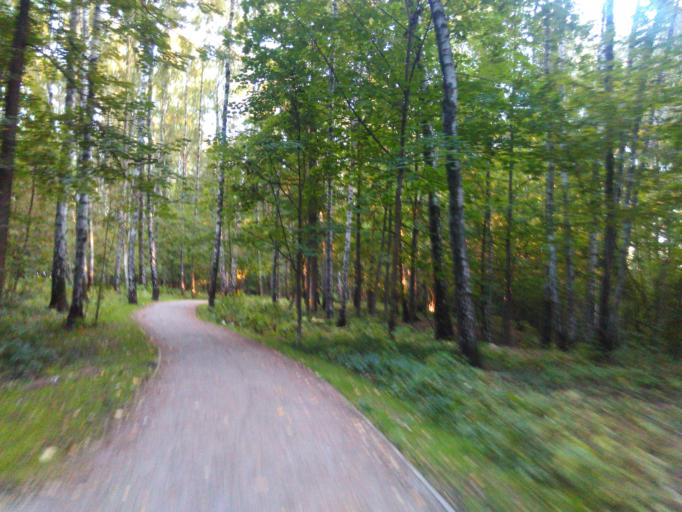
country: RU
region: Moscow
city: Troparevo
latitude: 55.6549
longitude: 37.5036
